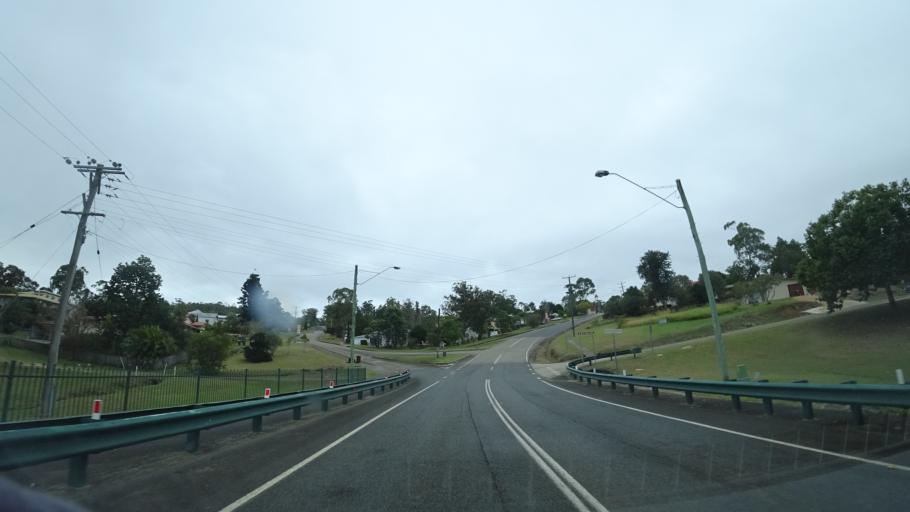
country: AU
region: Queensland
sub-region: Tablelands
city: Atherton
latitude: -17.3819
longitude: 145.3842
